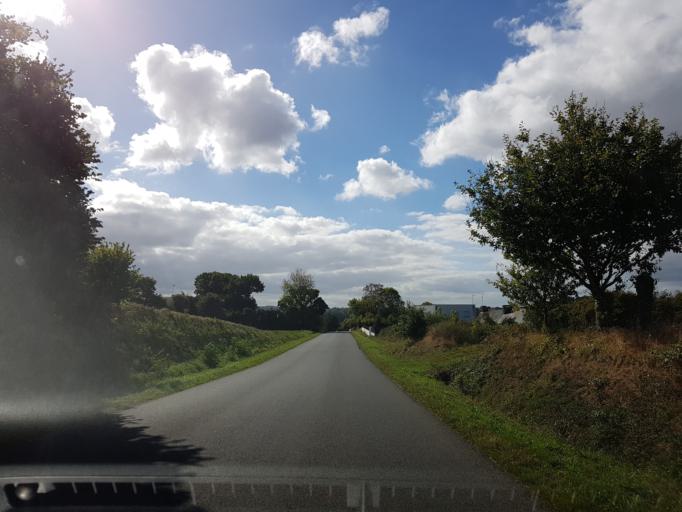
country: FR
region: Brittany
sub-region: Departement des Cotes-d'Armor
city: Pledran
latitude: 48.4603
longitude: -2.7520
